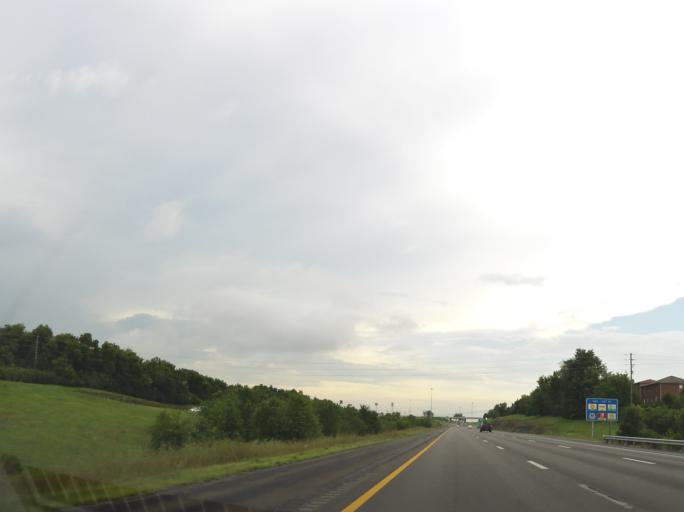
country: US
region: Kentucky
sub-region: Madison County
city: Richmond
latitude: 37.7273
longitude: -84.3225
